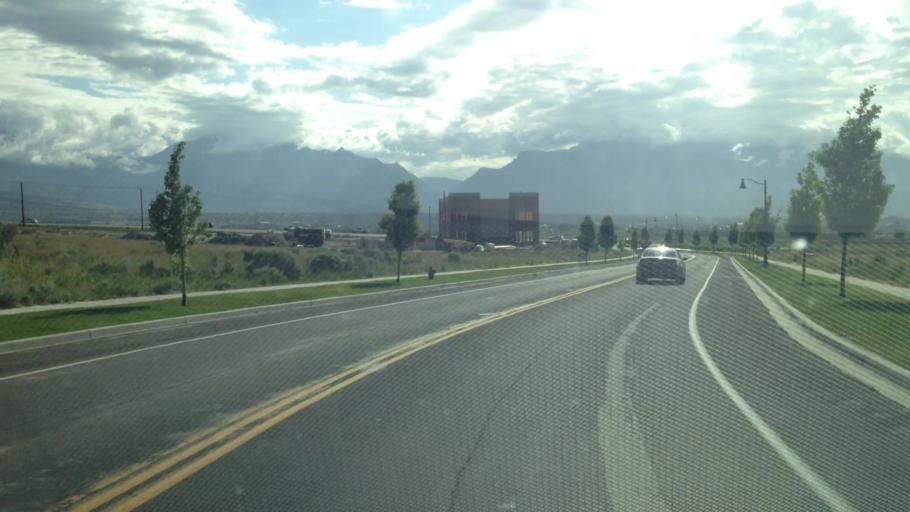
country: US
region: Utah
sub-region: Utah County
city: Saratoga Springs
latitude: 40.3948
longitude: -111.9214
